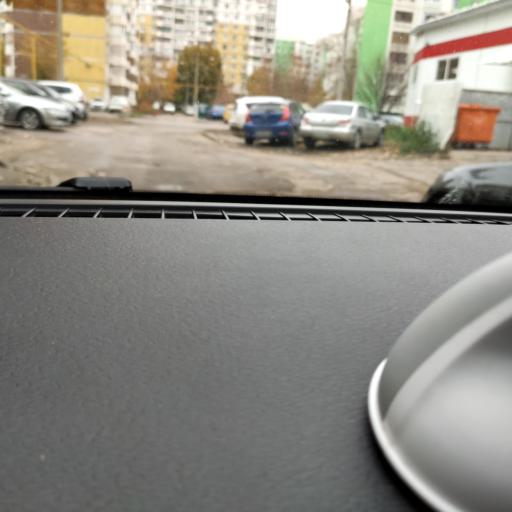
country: RU
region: Samara
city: Samara
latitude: 53.2571
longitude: 50.2091
